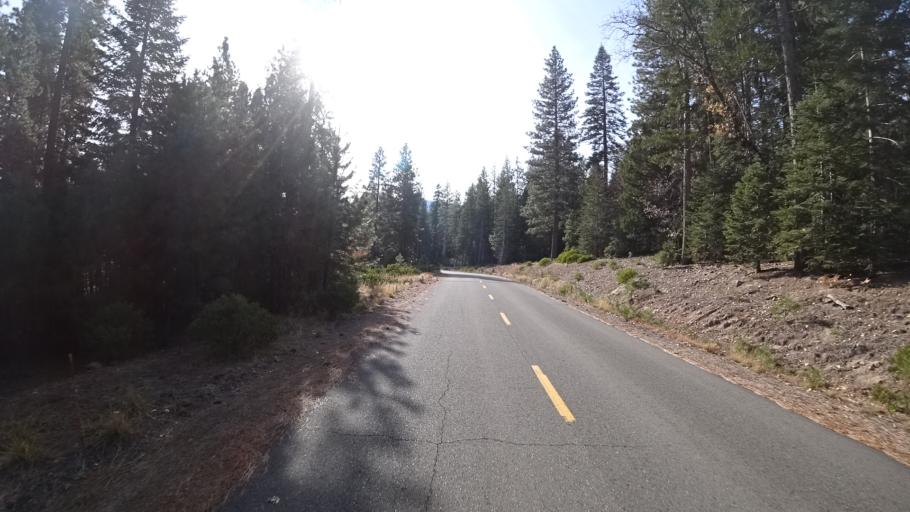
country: US
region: California
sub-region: Siskiyou County
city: Weed
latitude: 41.4009
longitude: -122.3885
